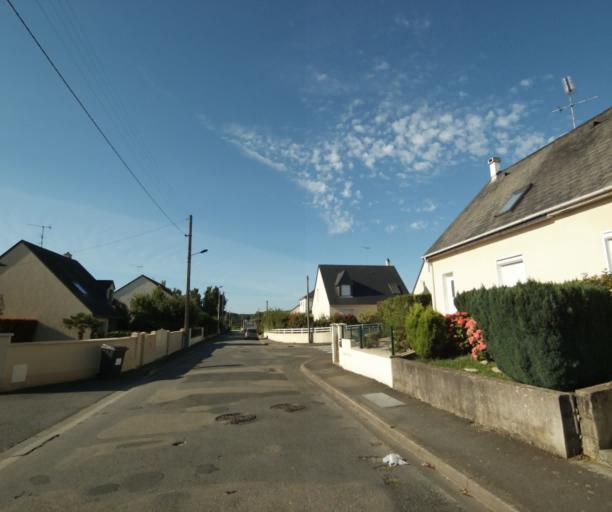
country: FR
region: Pays de la Loire
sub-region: Departement de la Mayenne
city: Laval
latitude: 48.0563
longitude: -0.7626
